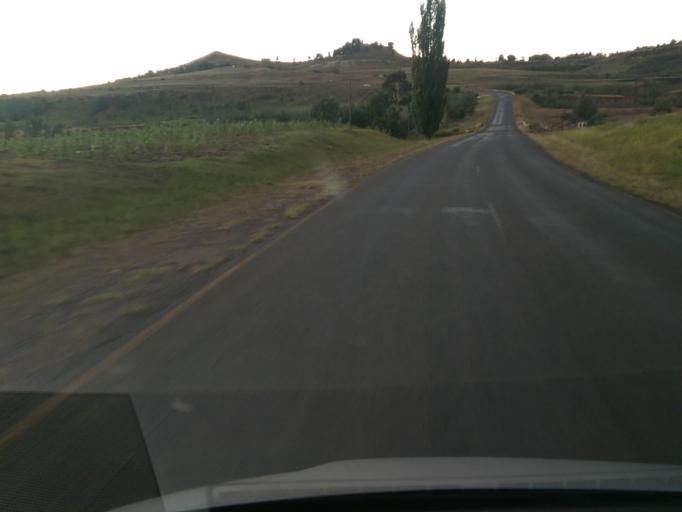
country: LS
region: Maseru
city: Nako
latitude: -29.4374
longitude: 27.6919
